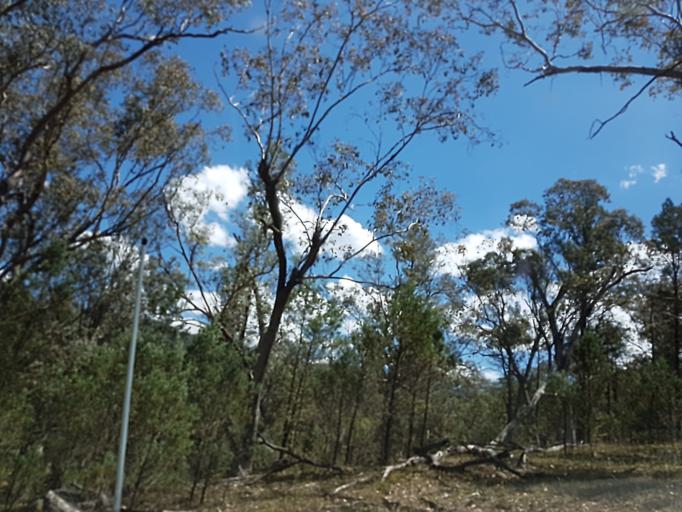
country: AU
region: New South Wales
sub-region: Snowy River
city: Jindabyne
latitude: -36.9434
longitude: 148.3840
